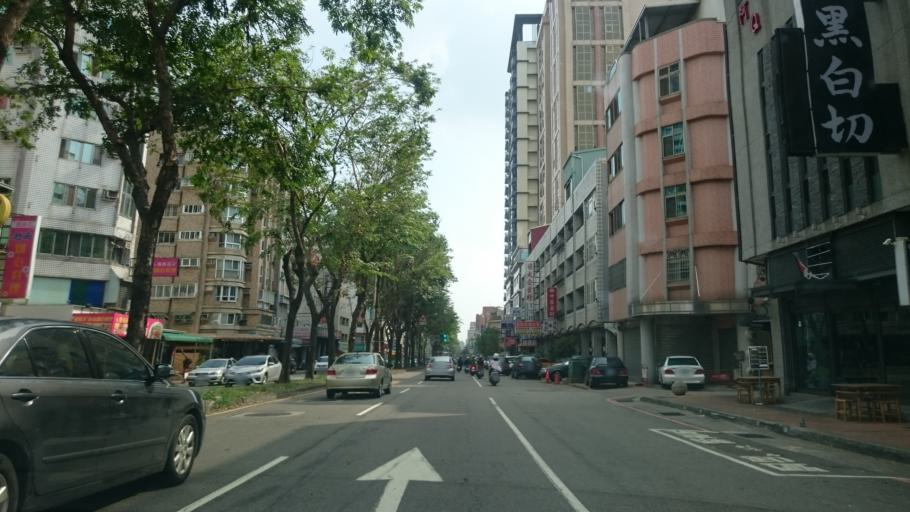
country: TW
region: Taiwan
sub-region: Taichung City
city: Taichung
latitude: 24.1393
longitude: 120.6573
